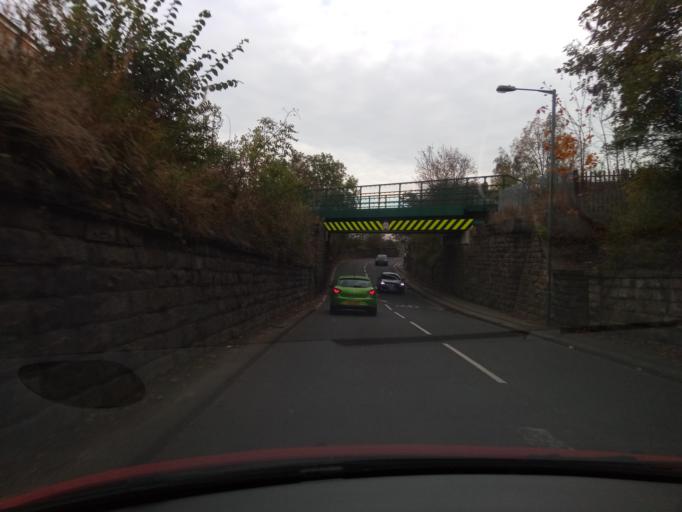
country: GB
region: England
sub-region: County Durham
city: Bishop Auckland
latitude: 54.6572
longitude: -1.6711
